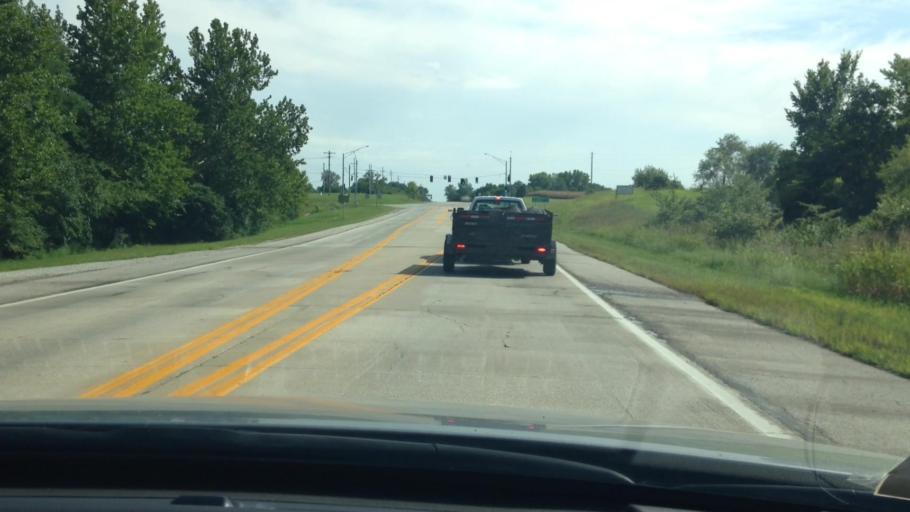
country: US
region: Missouri
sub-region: Cass County
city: Belton
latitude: 38.8198
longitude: -94.5857
